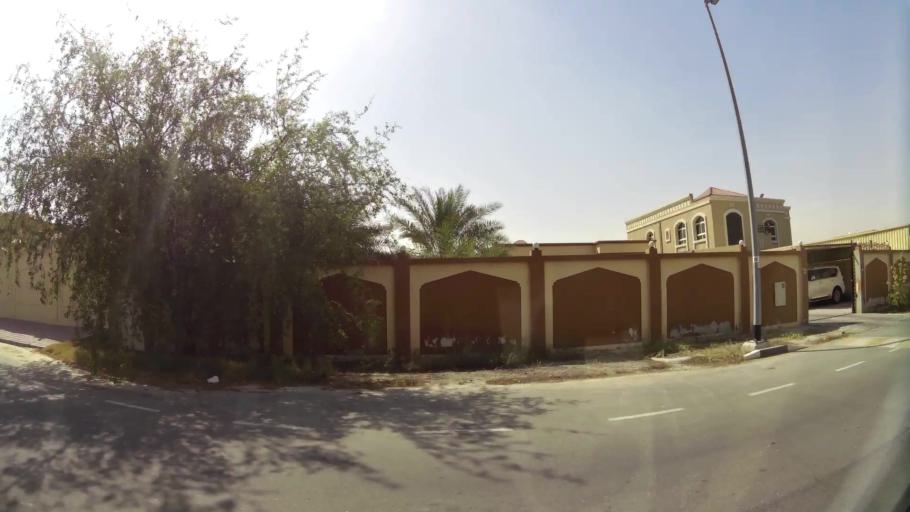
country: AE
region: Ash Shariqah
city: Sharjah
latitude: 25.2716
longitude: 55.3998
